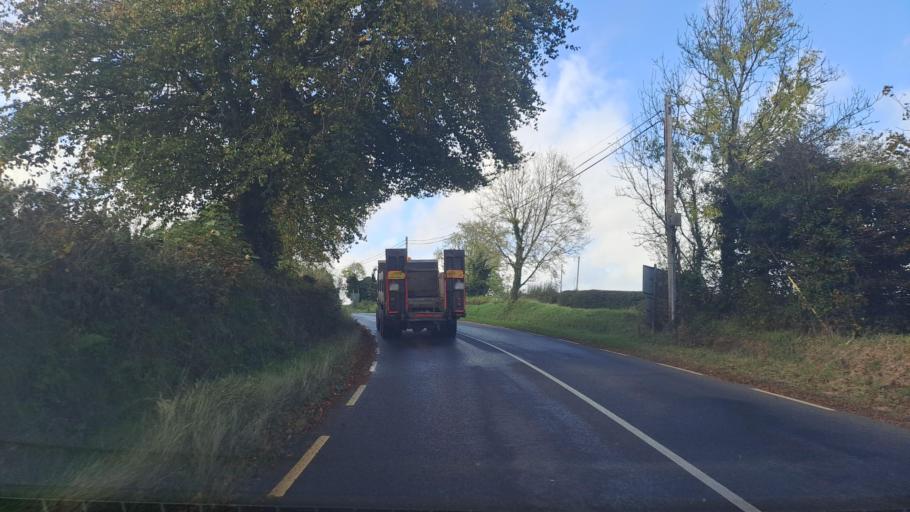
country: IE
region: Ulster
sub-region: County Monaghan
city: Monaghan
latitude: 54.1200
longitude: -6.9106
